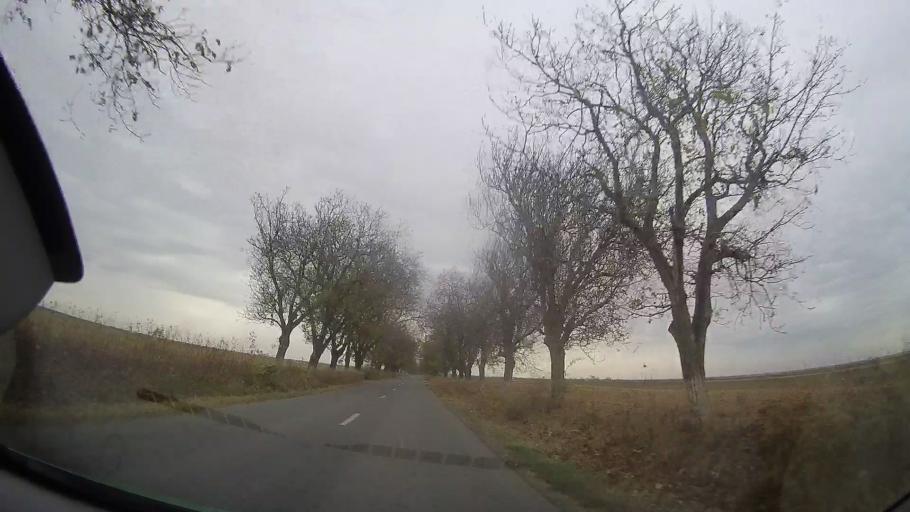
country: RO
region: Prahova
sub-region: Comuna Fantanele
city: Fantanele
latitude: 45.0162
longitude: 26.4027
